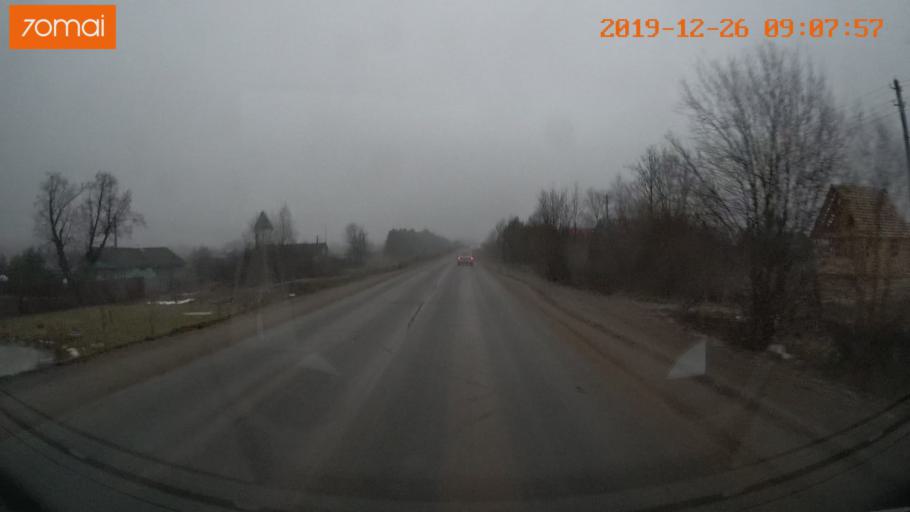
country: RU
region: Vologda
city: Gryazovets
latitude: 58.8514
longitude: 40.2470
